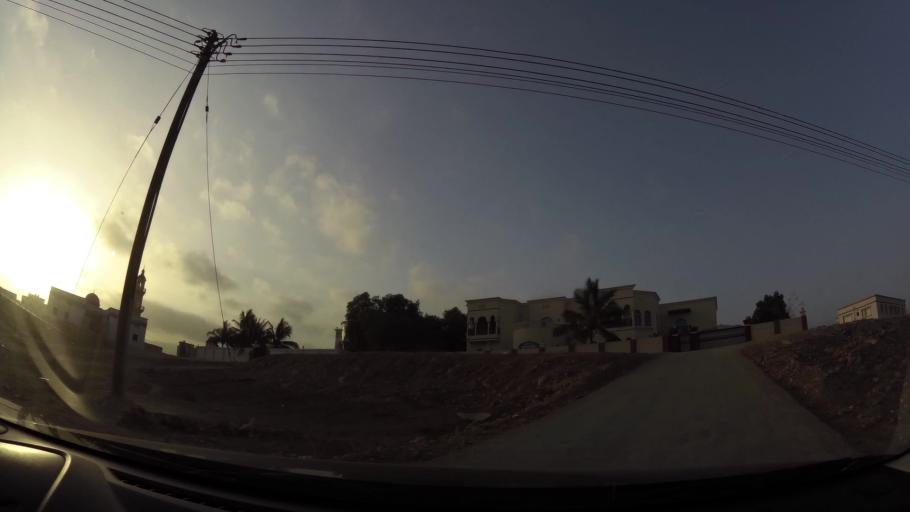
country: OM
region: Zufar
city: Salalah
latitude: 17.0046
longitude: 54.0346
